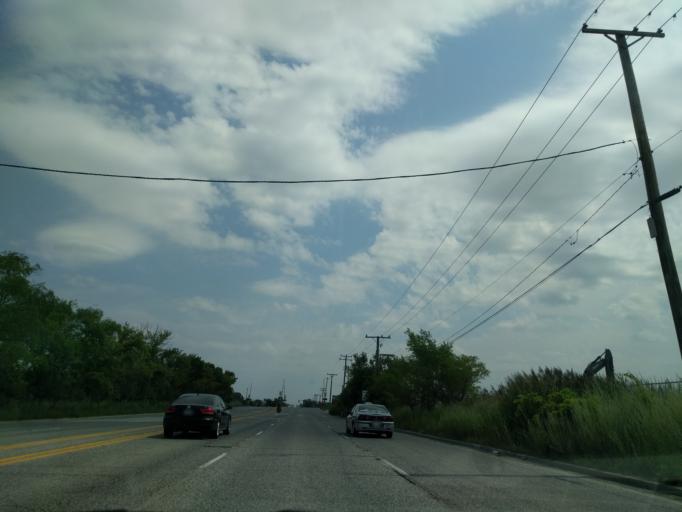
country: US
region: Illinois
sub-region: Cook County
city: Elk Grove Village
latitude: 42.0083
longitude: -87.9273
